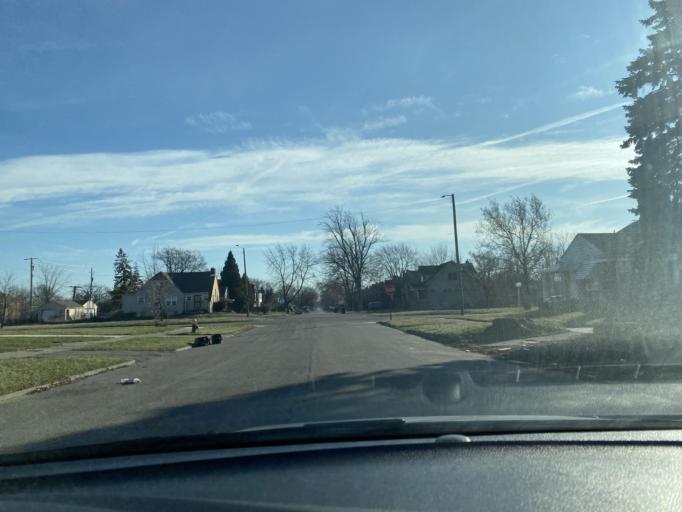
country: US
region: Michigan
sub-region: Wayne County
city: Grosse Pointe Park
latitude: 42.4053
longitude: -82.9503
